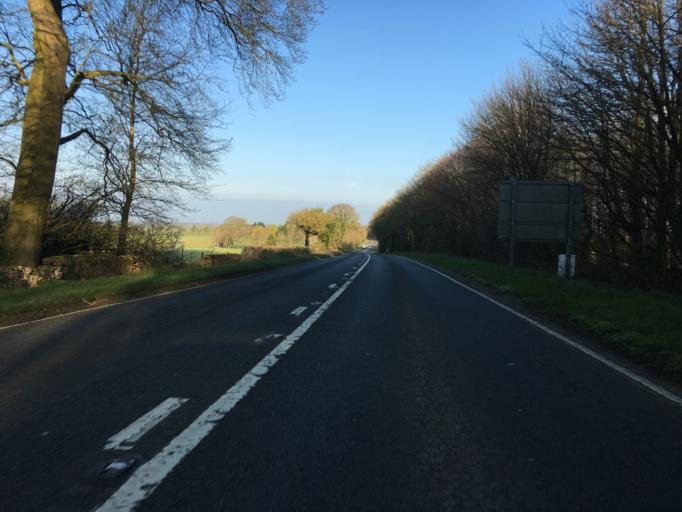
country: GB
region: England
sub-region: Gloucestershire
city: Bourton on the Water
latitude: 51.8235
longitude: -1.7797
